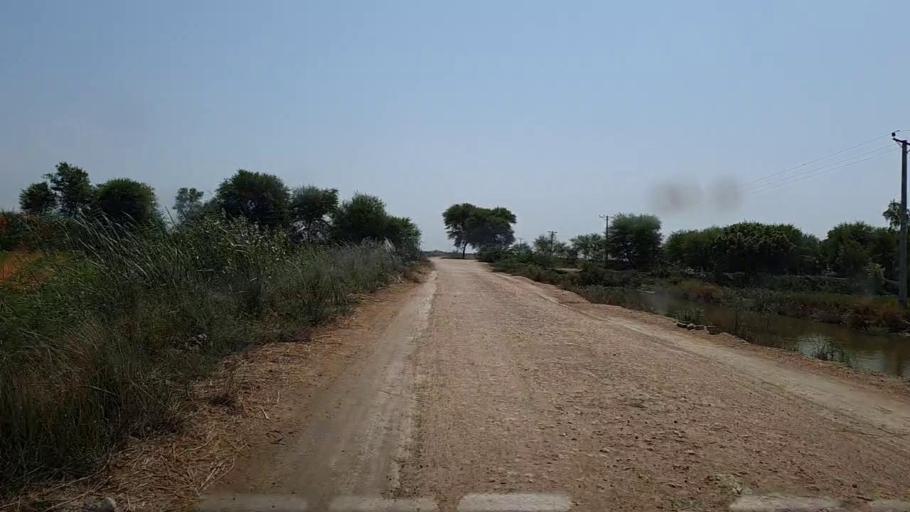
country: PK
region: Sindh
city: Mirpur Batoro
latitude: 24.6412
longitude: 68.4522
